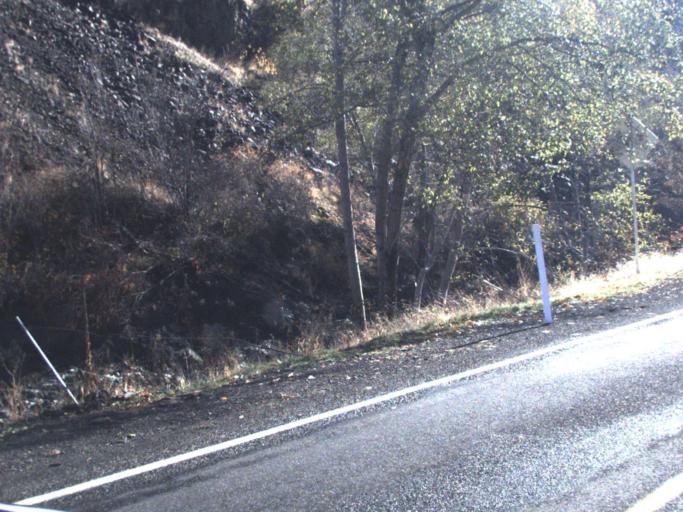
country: US
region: Washington
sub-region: Asotin County
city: Asotin
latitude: 46.0548
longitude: -117.2384
